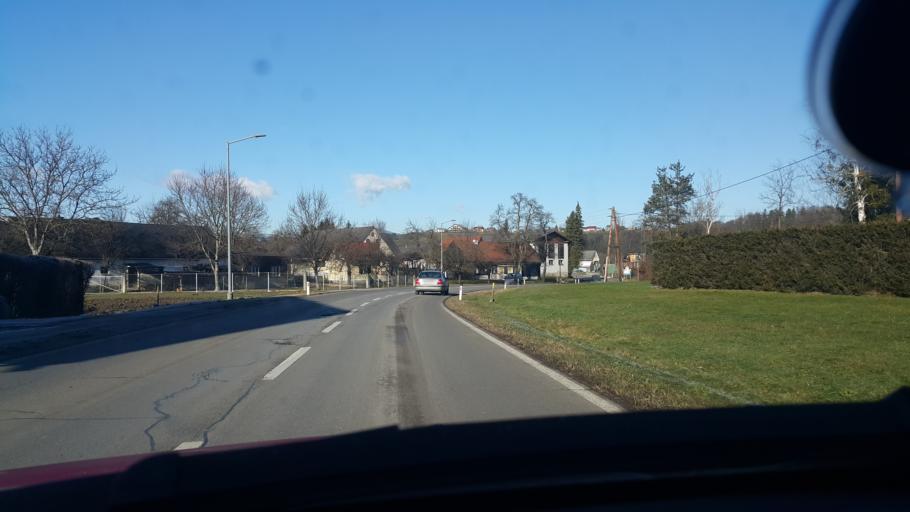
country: AT
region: Styria
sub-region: Politischer Bezirk Deutschlandsberg
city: Sankt Martin im Sulmtal
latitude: 46.7634
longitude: 15.2825
